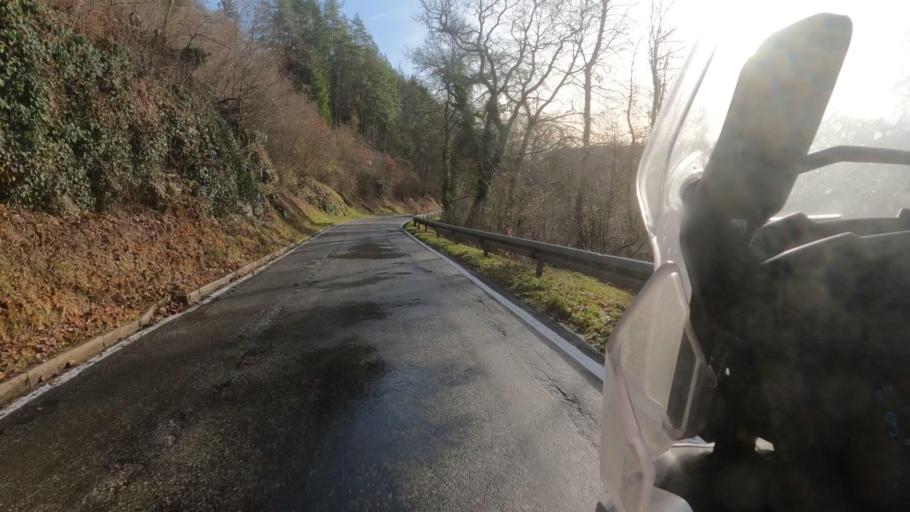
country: DE
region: Baden-Wuerttemberg
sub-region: Freiburg Region
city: Tengen
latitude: 47.8092
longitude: 8.6588
